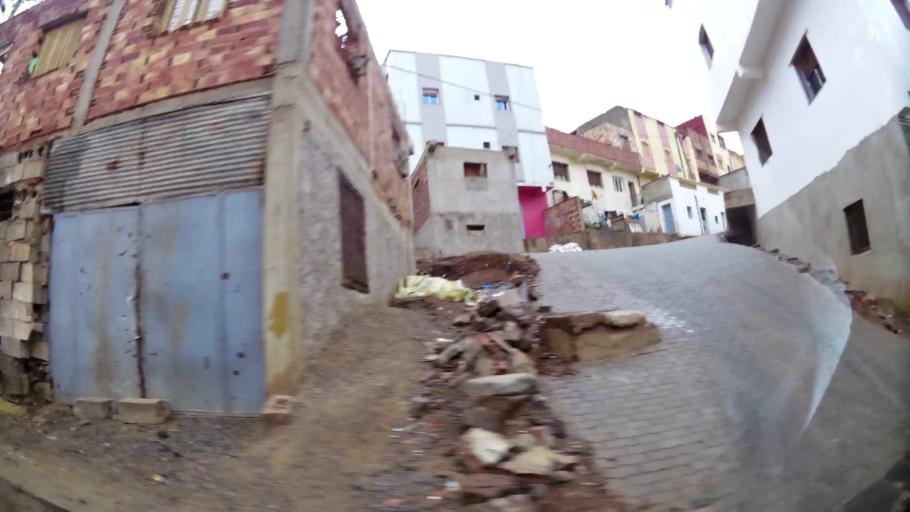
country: MA
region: Oriental
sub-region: Nador
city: Nador
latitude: 35.1819
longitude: -2.9362
